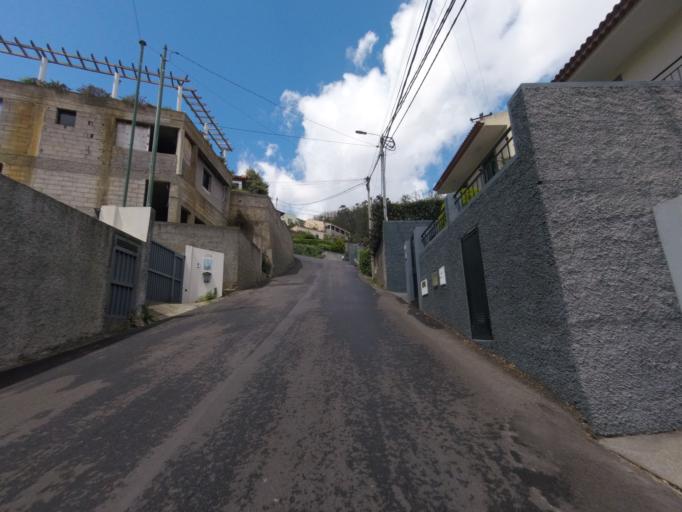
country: PT
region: Madeira
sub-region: Funchal
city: Nossa Senhora do Monte
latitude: 32.6786
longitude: -16.9202
